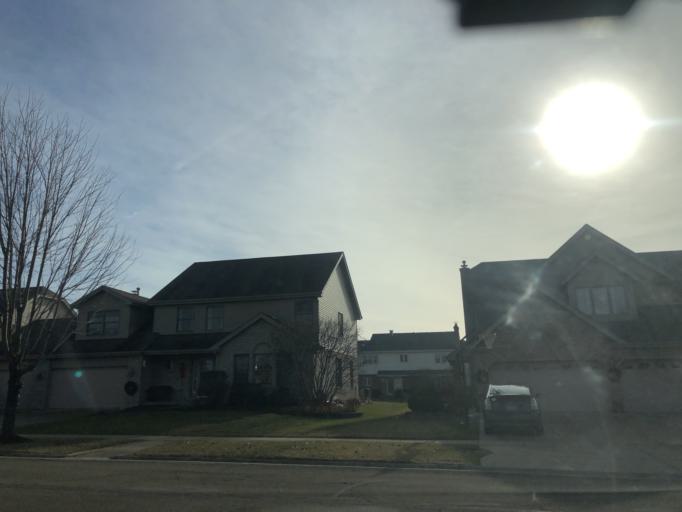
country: US
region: Illinois
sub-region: DuPage County
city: Woodridge
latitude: 41.7166
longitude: -88.0239
